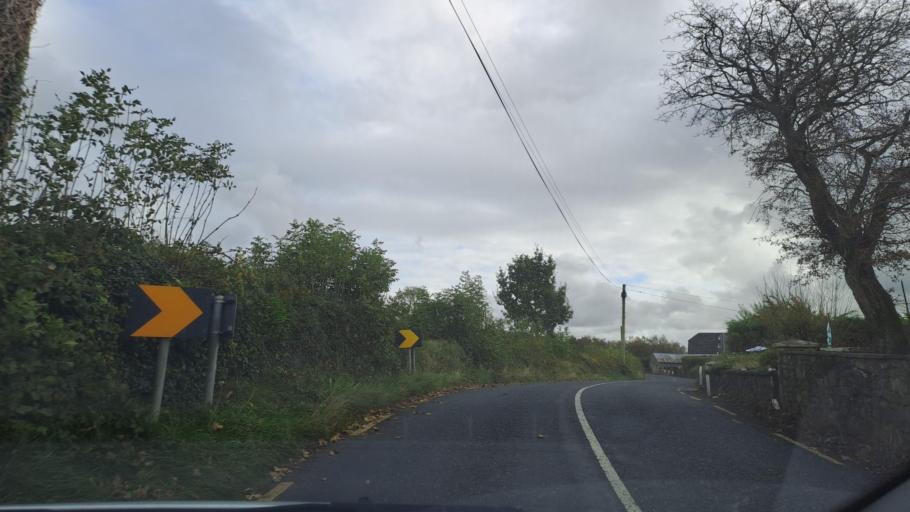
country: IE
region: Ulster
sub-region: An Cabhan
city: Virginia
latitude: 53.8296
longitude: -7.0570
